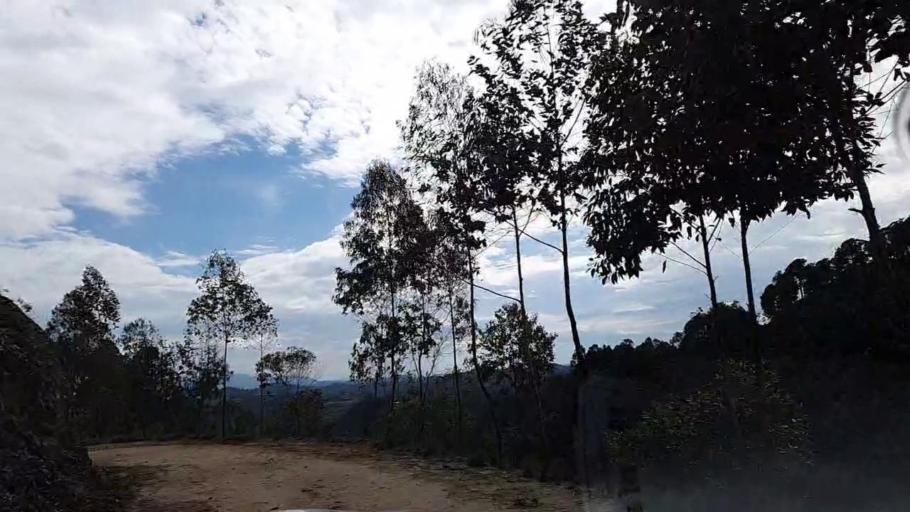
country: RW
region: Southern Province
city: Nzega
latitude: -2.4113
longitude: 29.4567
